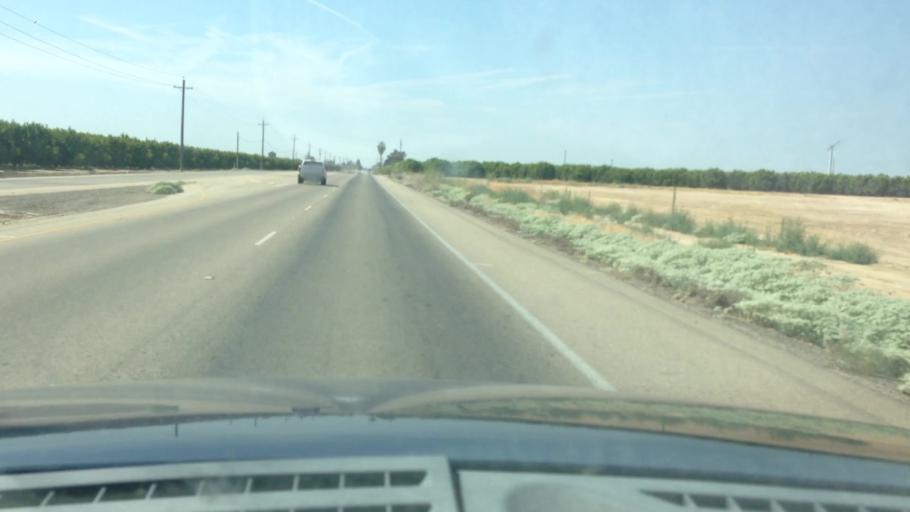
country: US
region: California
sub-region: Fresno County
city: Parlier
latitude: 36.6316
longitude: -119.5567
